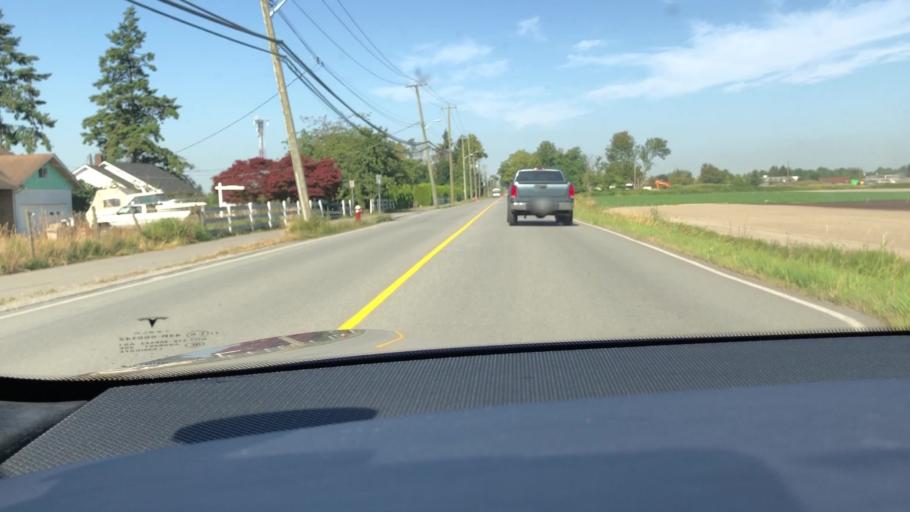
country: CA
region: British Columbia
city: Richmond
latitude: 49.1696
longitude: -123.0539
